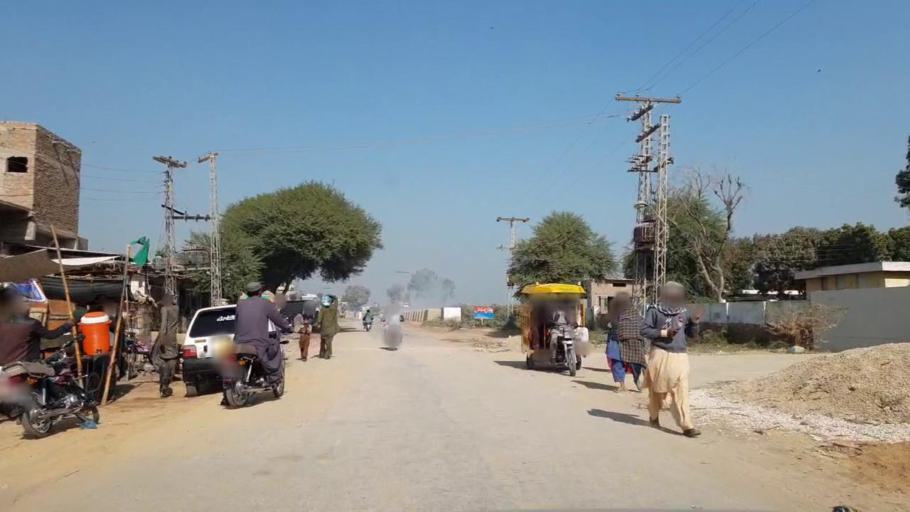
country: PK
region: Sindh
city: Tando Adam
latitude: 25.6357
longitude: 68.5945
